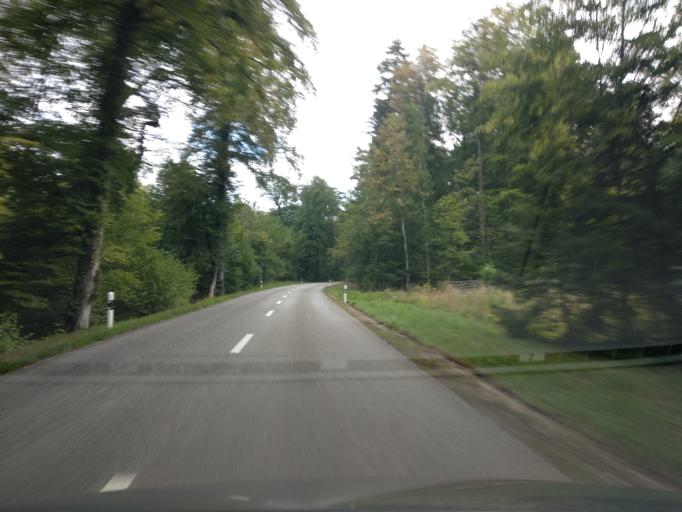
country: CH
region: Thurgau
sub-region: Frauenfeld District
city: Diessenhofen
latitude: 47.6772
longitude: 8.7224
